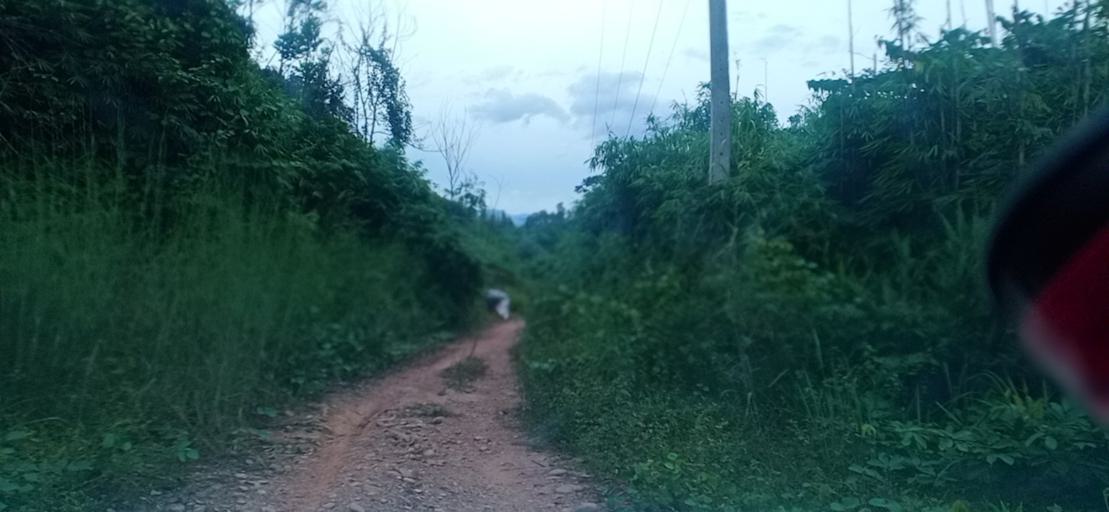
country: TH
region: Changwat Bueng Kan
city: Pak Khat
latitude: 18.5601
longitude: 103.2571
